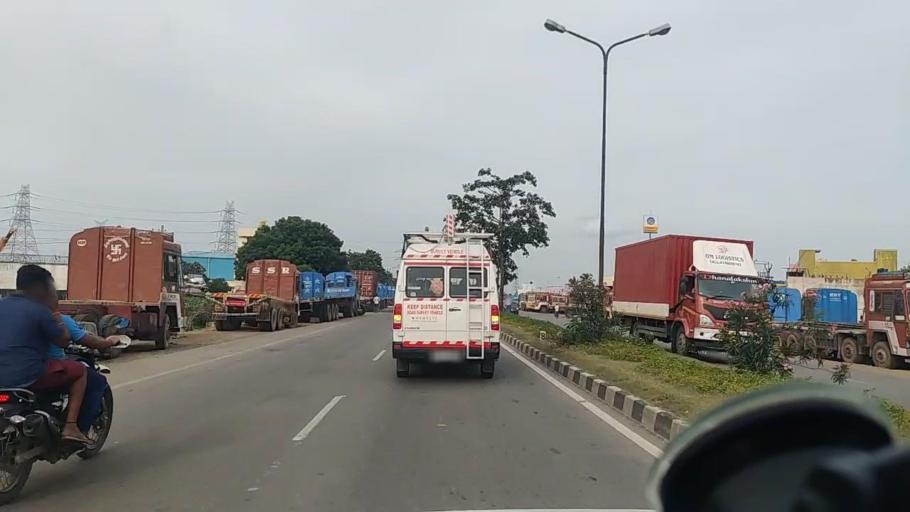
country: IN
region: Tamil Nadu
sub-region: Thiruvallur
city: Chinnasekkadu
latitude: 13.1785
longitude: 80.2500
